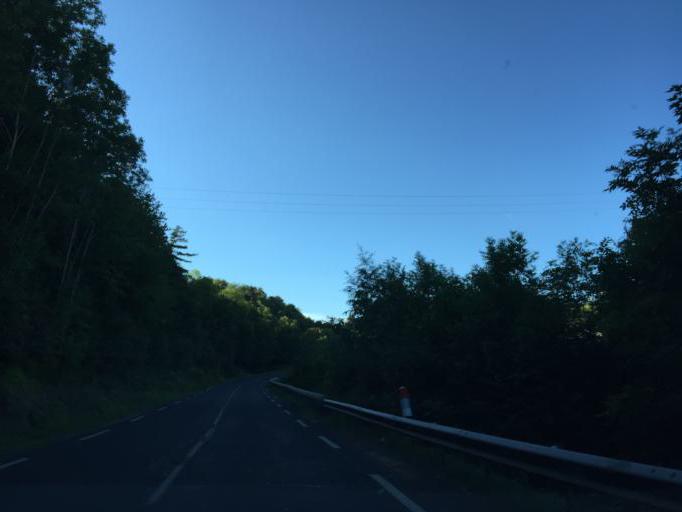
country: FR
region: Auvergne
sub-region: Departement de la Haute-Loire
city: Bains
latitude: 44.9926
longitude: 3.6817
